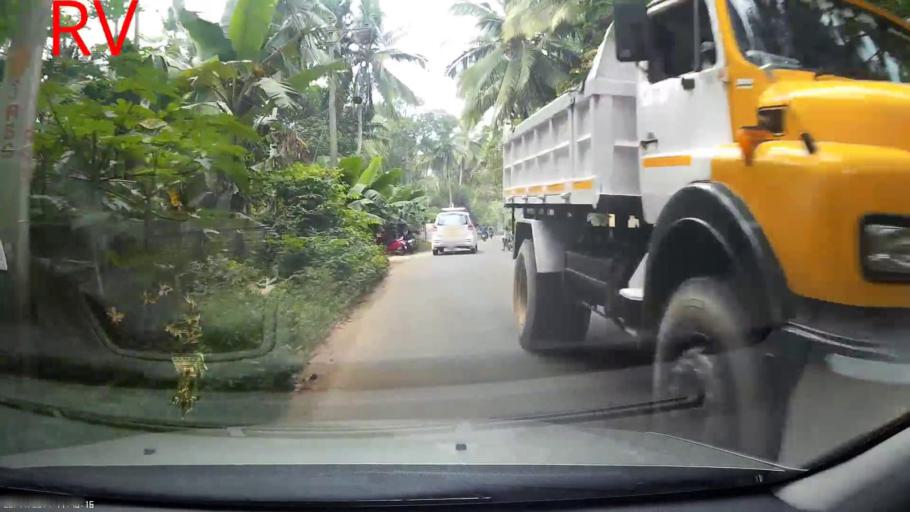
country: IN
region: Kerala
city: Kovalam
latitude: 8.3983
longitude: 77.0215
